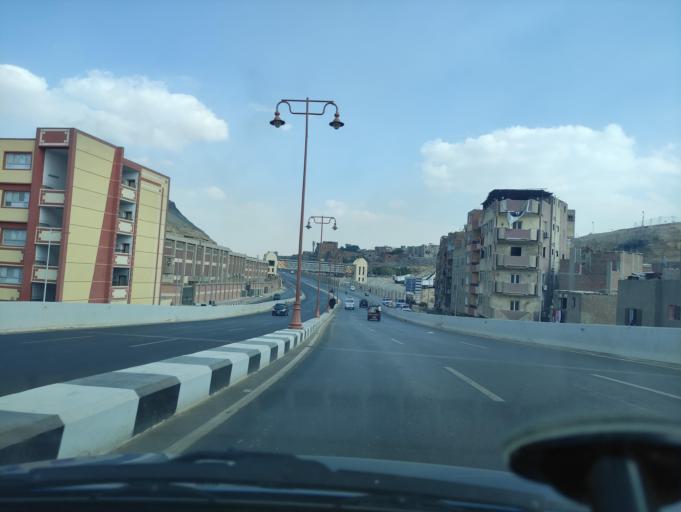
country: EG
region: Muhafazat al Qahirah
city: Cairo
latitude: 30.0474
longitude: 31.2874
